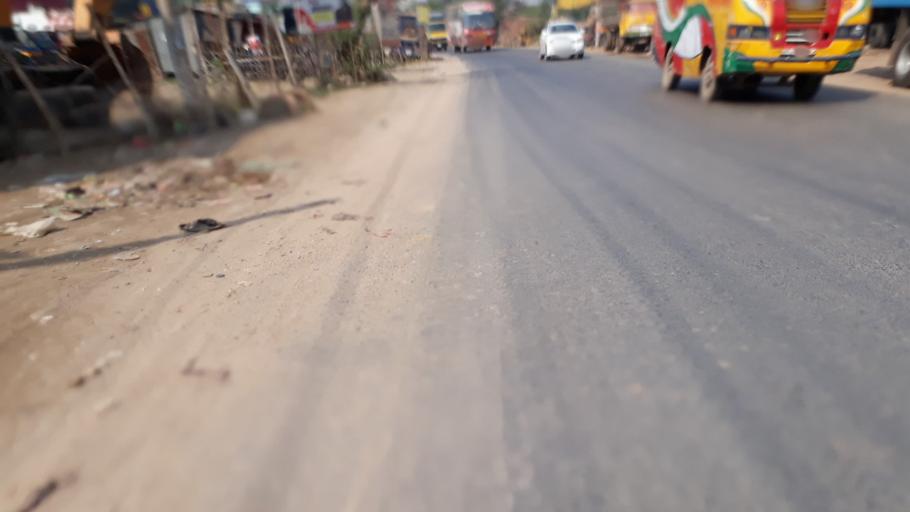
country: BD
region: Dhaka
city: Tungi
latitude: 23.9019
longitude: 90.3263
